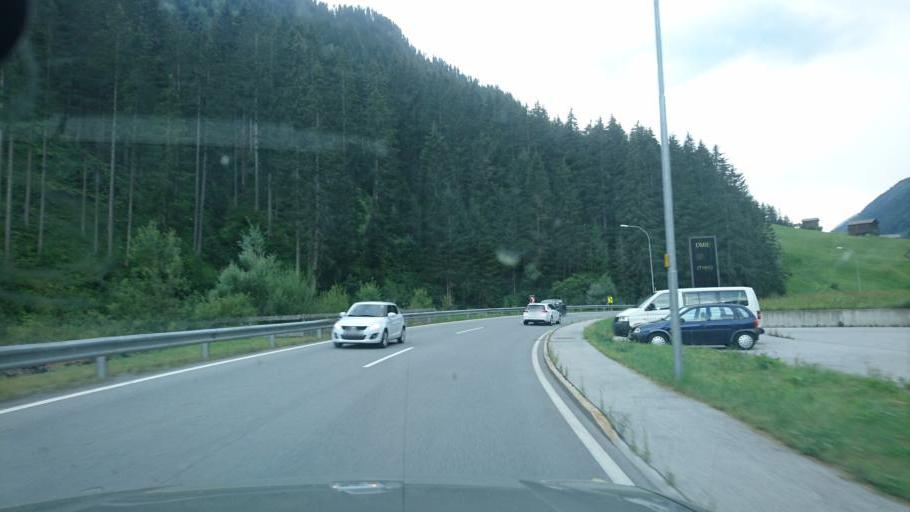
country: AT
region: Tyrol
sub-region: Politischer Bezirk Landeck
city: Kappl
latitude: 47.0509
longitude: 10.3546
